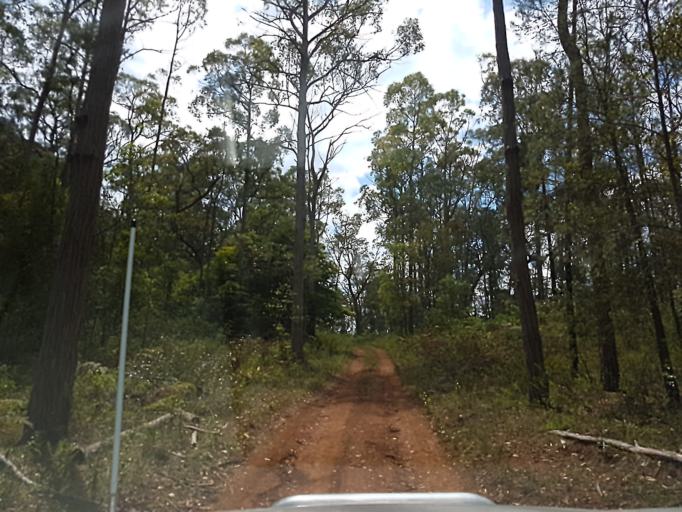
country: AU
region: Victoria
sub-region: East Gippsland
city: Lakes Entrance
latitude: -37.3490
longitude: 148.3573
